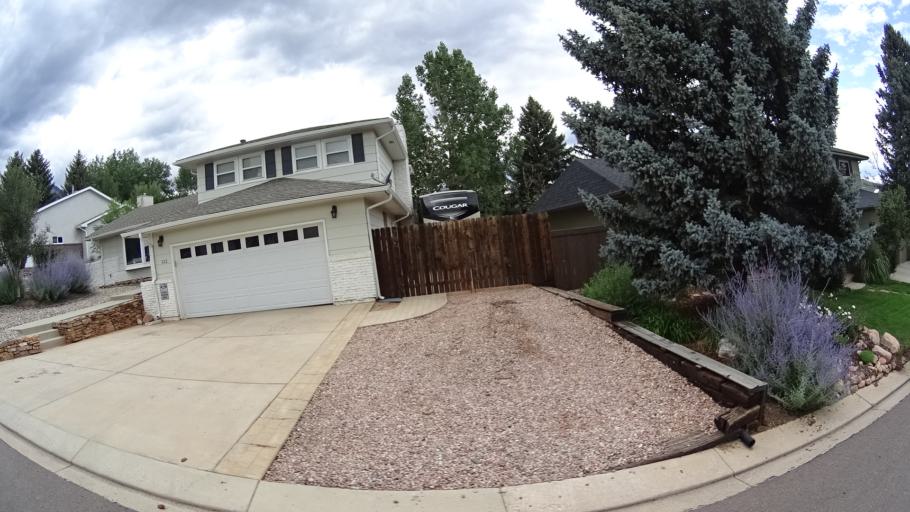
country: US
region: Colorado
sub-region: El Paso County
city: Manitou Springs
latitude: 38.8477
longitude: -104.8918
